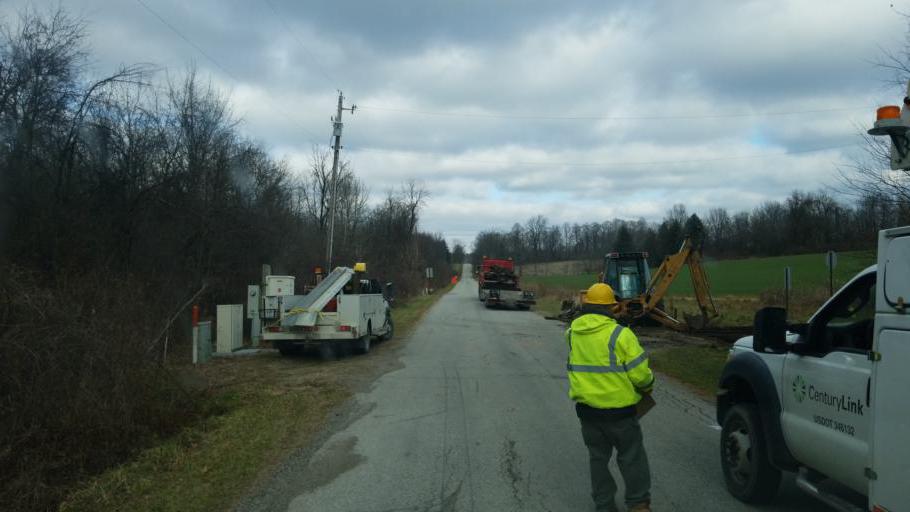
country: US
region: Ohio
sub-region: Richland County
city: Lexington
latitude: 40.6887
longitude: -82.6894
